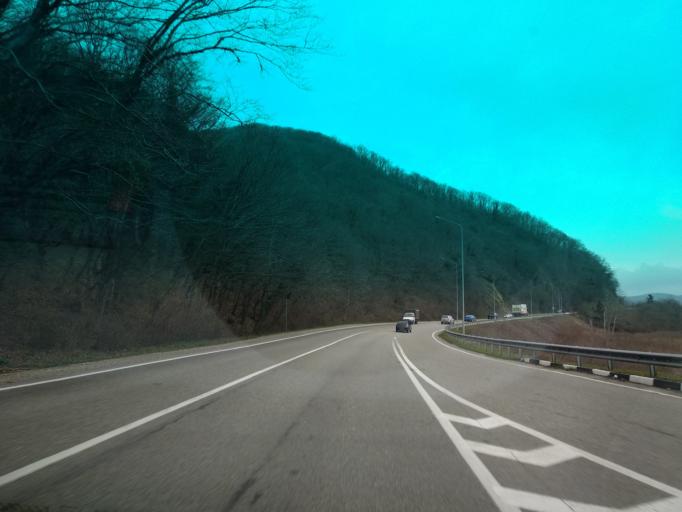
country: RU
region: Krasnodarskiy
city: Ol'ginka
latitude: 44.2177
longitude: 38.8942
